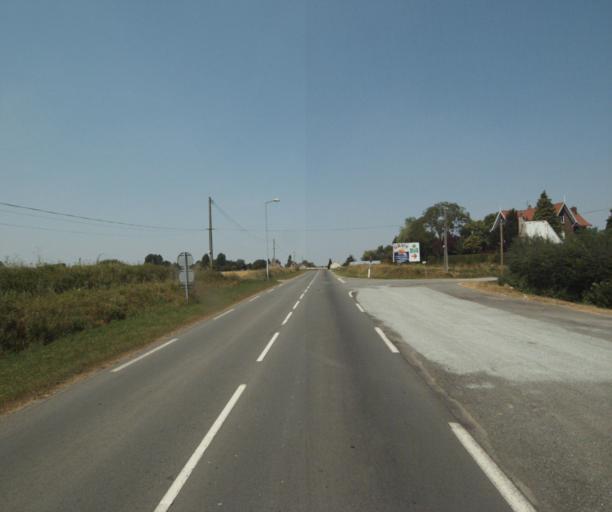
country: FR
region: Nord-Pas-de-Calais
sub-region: Departement du Nord
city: Wambrechies
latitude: 50.7036
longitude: 3.0351
